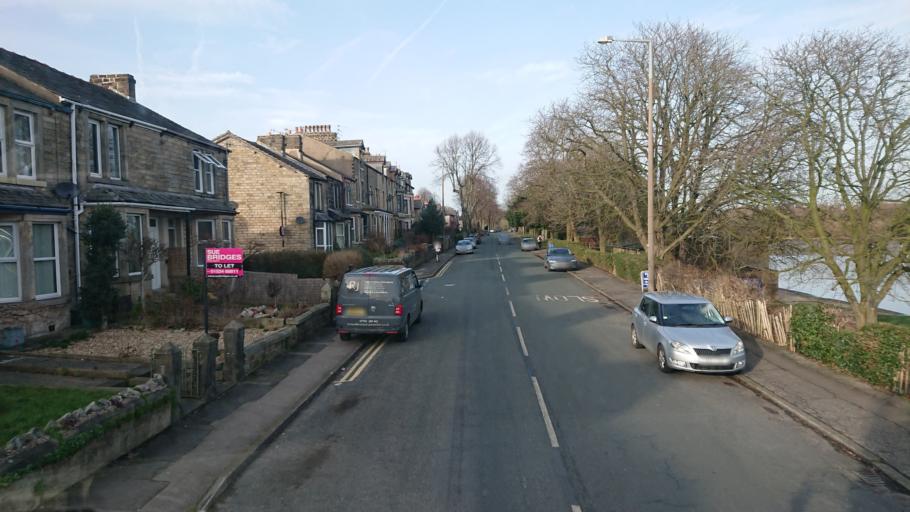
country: GB
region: England
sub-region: Lancashire
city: Lancaster
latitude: 54.0617
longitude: -2.7958
